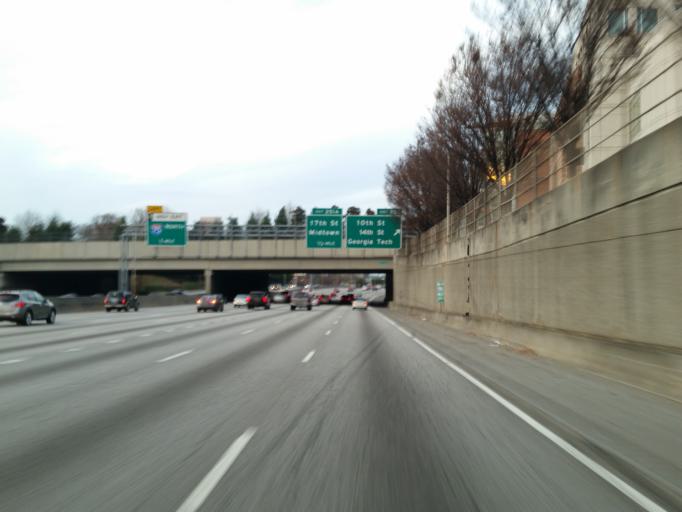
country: US
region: Georgia
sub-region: Fulton County
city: Atlanta
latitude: 33.7755
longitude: -84.3902
